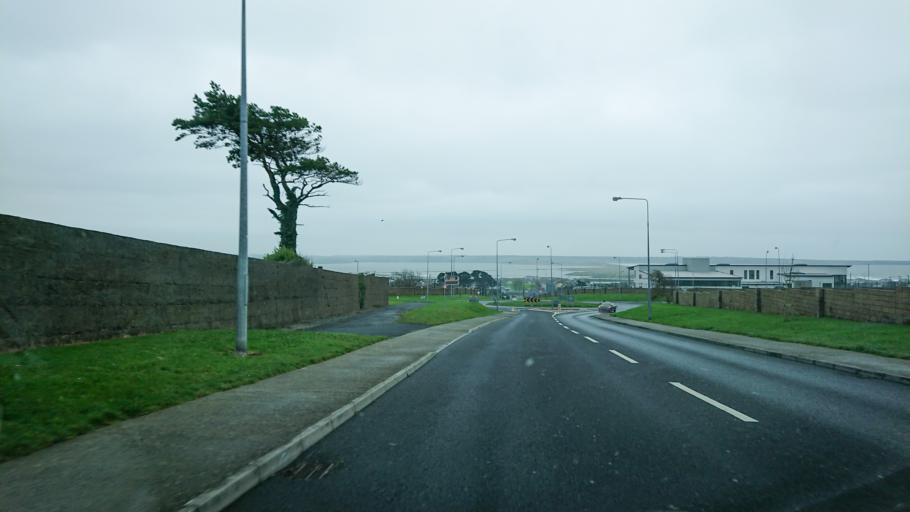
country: IE
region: Munster
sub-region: Waterford
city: Tra Mhor
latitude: 52.1702
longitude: -7.1488
